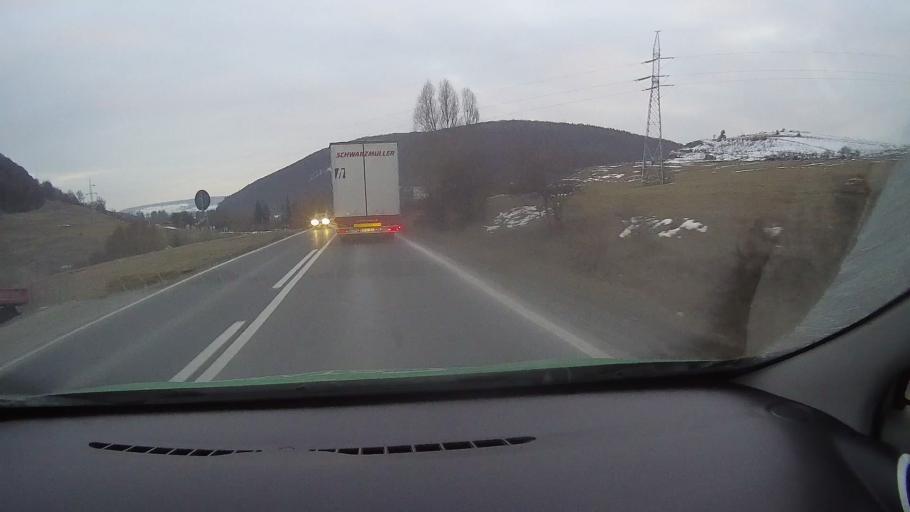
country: RO
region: Harghita
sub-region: Municipiul Odorheiu Secuiesc
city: Odorheiu Secuiesc
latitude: 46.3384
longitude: 25.2698
